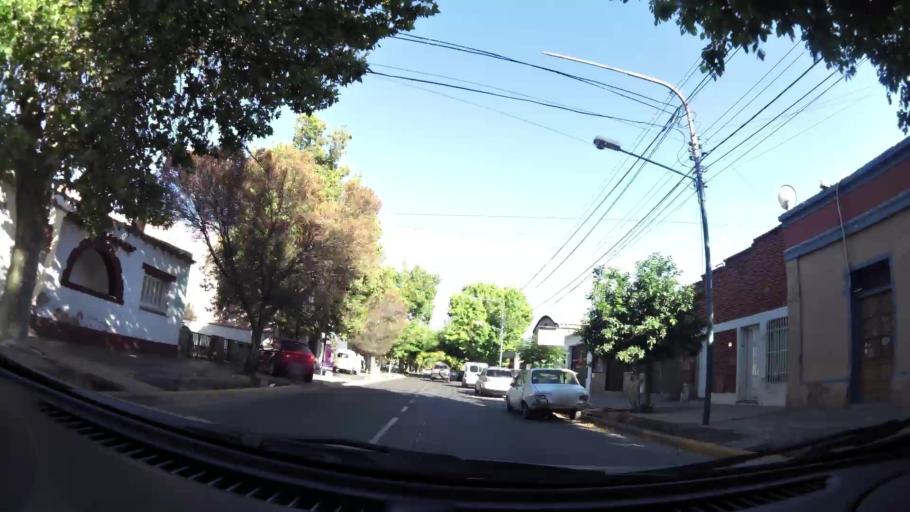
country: AR
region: Mendoza
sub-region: Departamento de Godoy Cruz
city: Godoy Cruz
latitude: -32.9299
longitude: -68.8427
